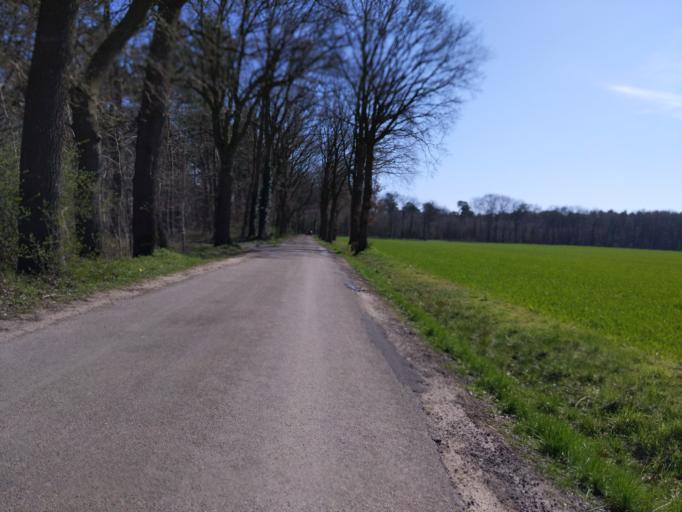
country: DE
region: North Rhine-Westphalia
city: Dorsten
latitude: 51.6950
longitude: 6.9758
